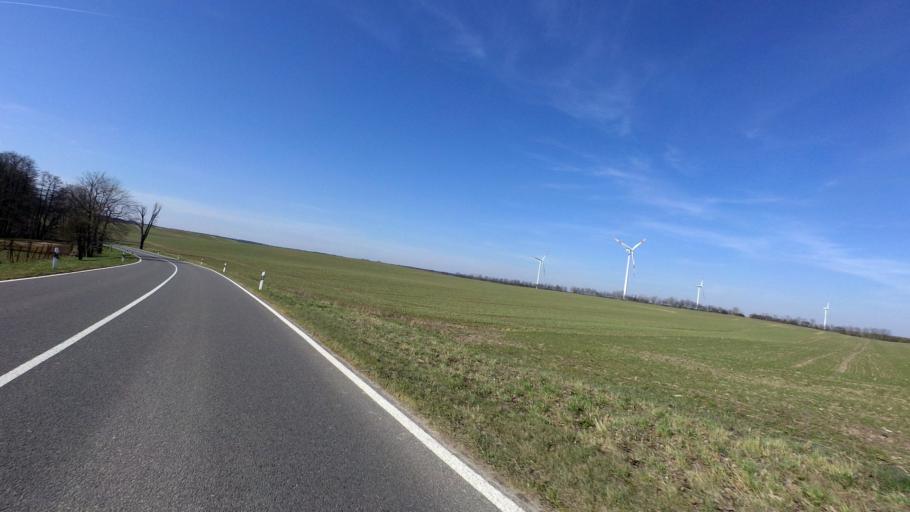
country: DE
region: Brandenburg
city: Protzel
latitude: 52.6334
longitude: 14.0101
